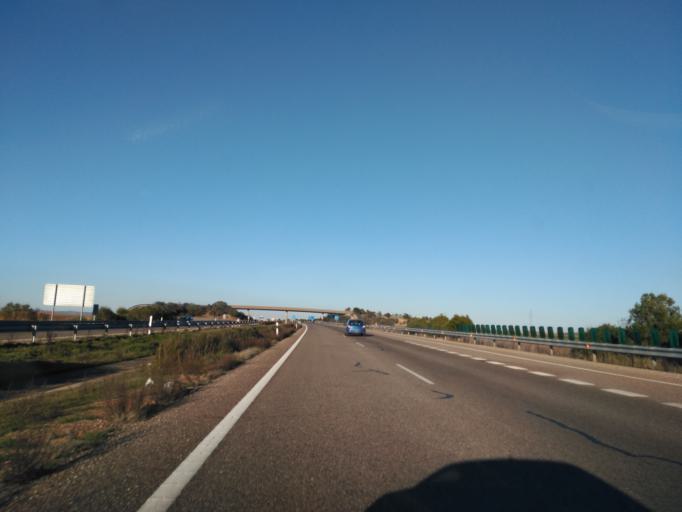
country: ES
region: Castille and Leon
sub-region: Provincia de Salamanca
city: Castellanos de Moriscos
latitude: 41.0319
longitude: -5.5688
